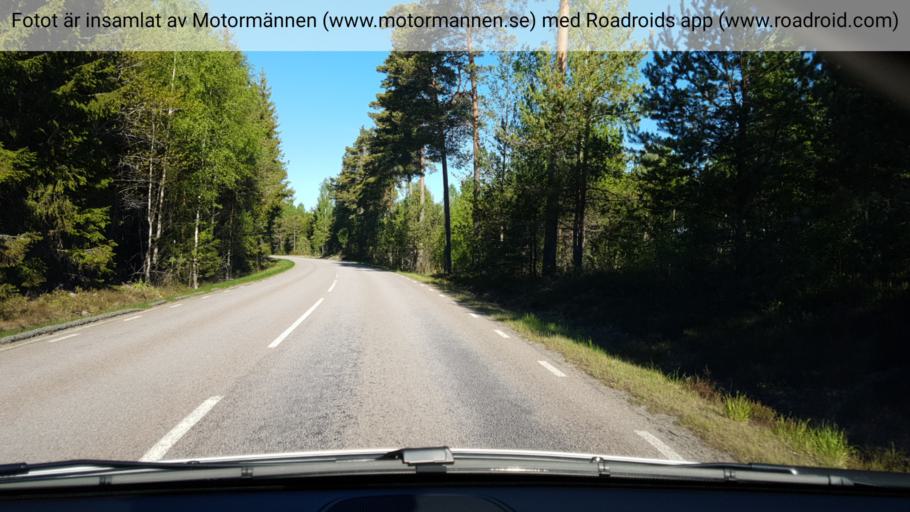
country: SE
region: Vaestra Goetaland
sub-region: Gotene Kommun
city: Goetene
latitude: 58.5448
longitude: 13.6766
